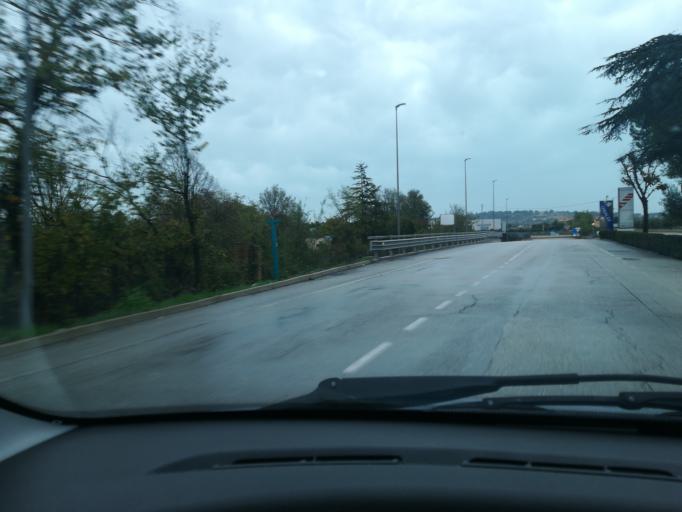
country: IT
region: The Marches
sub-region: Provincia di Macerata
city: Borgo Stazione
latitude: 43.2884
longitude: 13.6512
